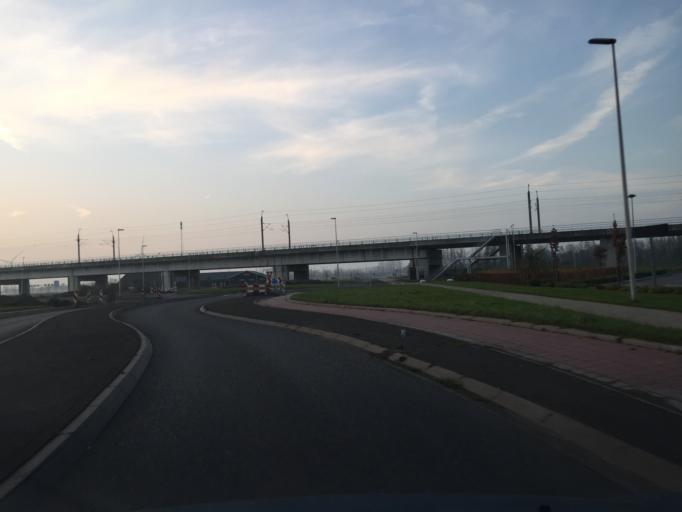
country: NL
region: South Holland
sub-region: Gemeente Lansingerland
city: Bleiswijk
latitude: 52.0412
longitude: 4.5338
